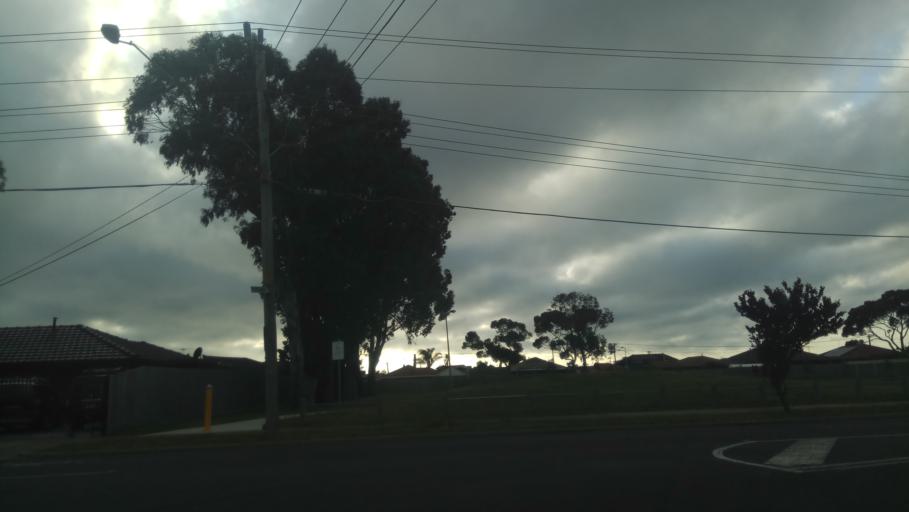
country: AU
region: Victoria
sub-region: Hobsons Bay
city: Altona Meadows
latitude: -37.8836
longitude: 144.7850
